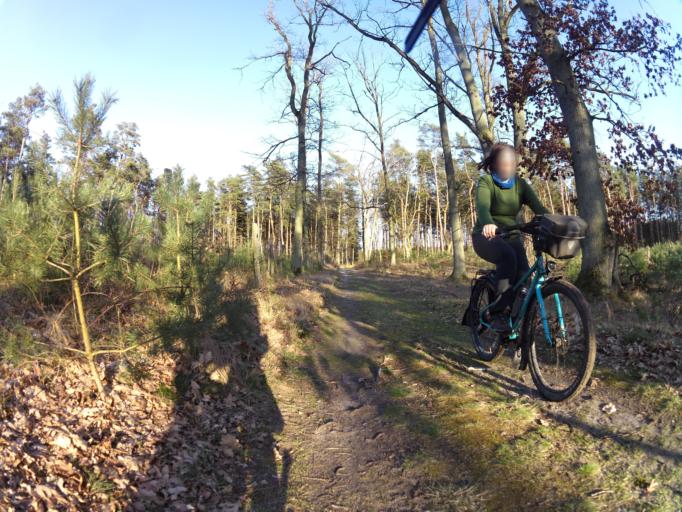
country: PL
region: West Pomeranian Voivodeship
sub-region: Powiat policki
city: Nowe Warpno
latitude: 53.7335
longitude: 14.3178
